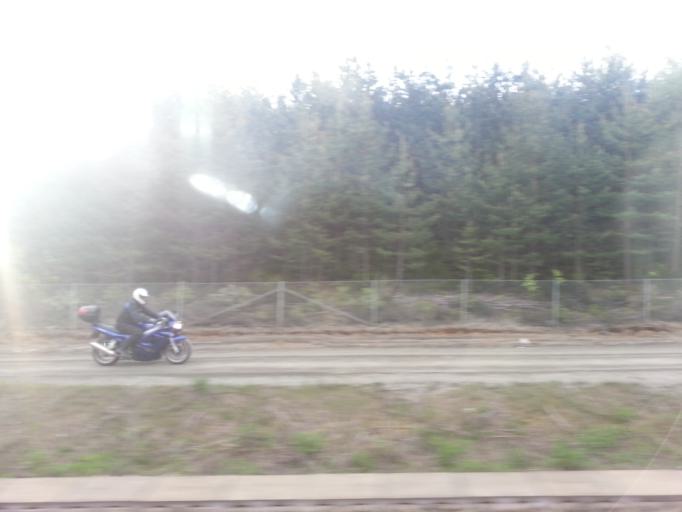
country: NO
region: Akershus
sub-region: Nannestad
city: Teigebyen
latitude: 60.1867
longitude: 11.0930
